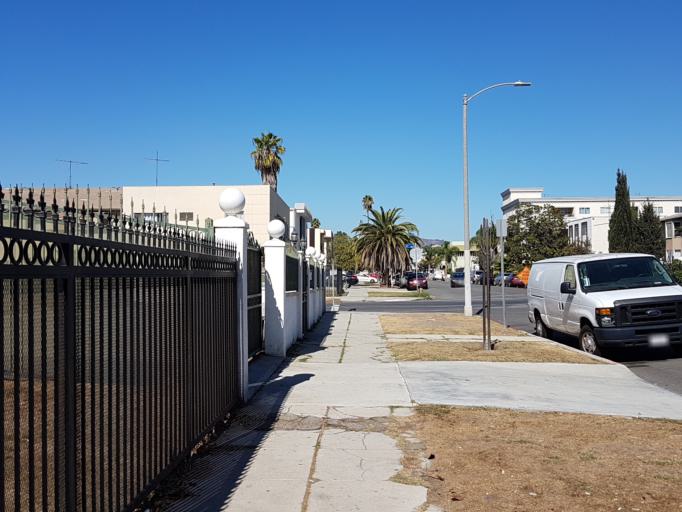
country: US
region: California
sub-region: Los Angeles County
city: Hollywood
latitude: 34.0668
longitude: -118.3067
